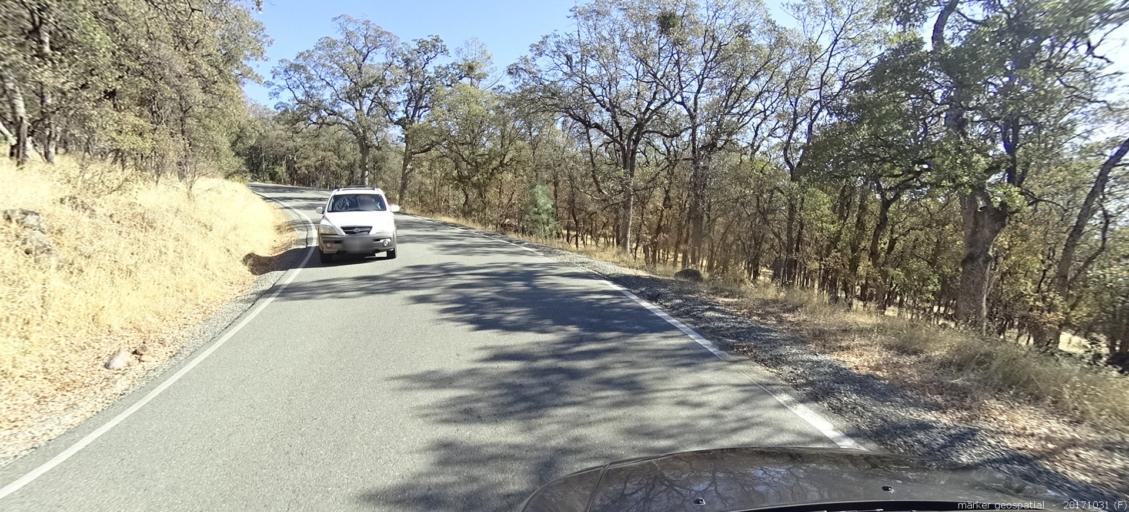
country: US
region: California
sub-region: Shasta County
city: Shingletown
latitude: 40.4588
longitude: -121.8972
